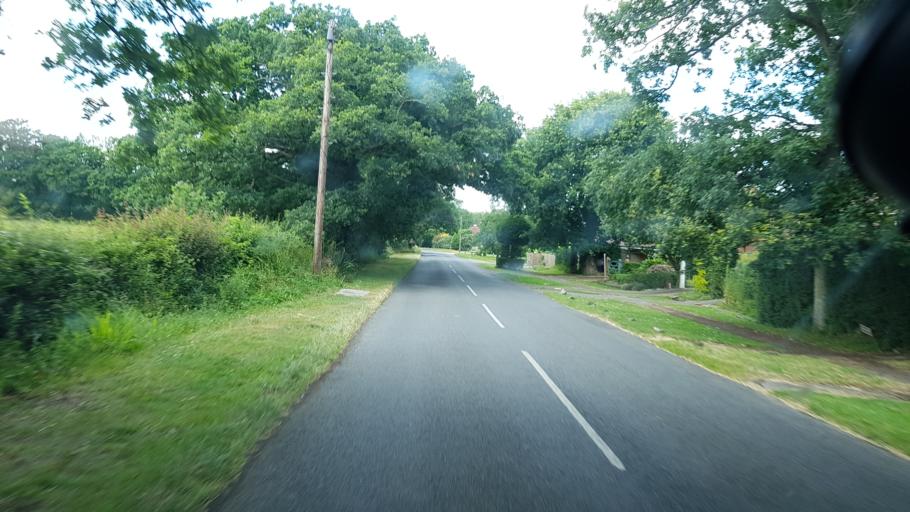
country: GB
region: England
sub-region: West Sussex
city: Rudgwick
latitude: 51.0798
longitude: -0.4535
